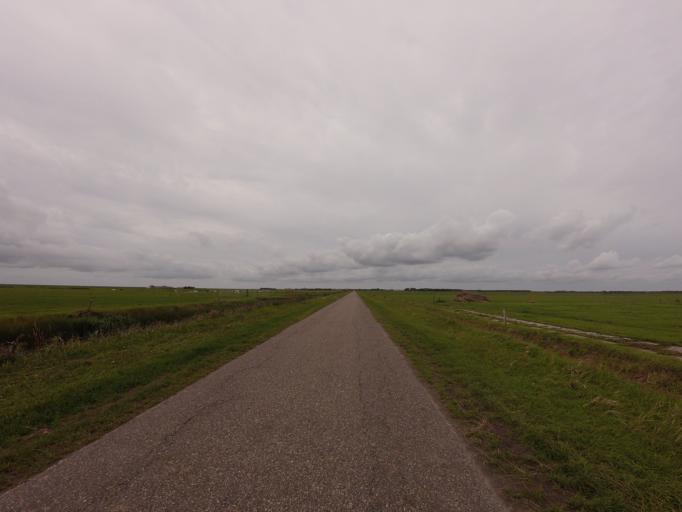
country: NL
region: Friesland
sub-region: Gemeente Ameland
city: Hollum
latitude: 53.4318
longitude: 5.6883
